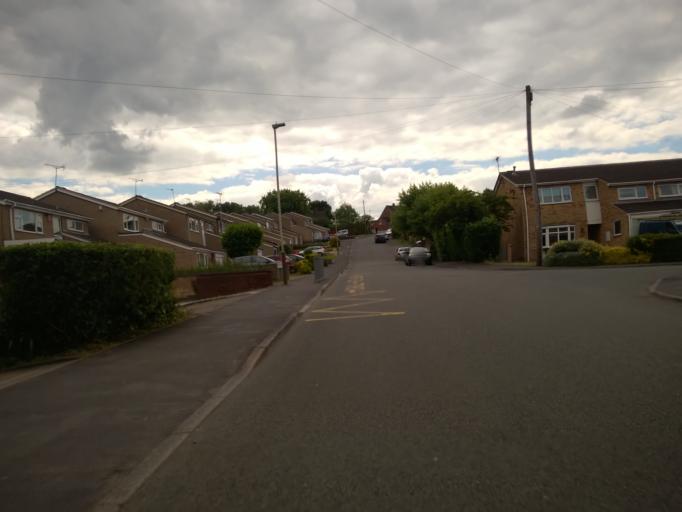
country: GB
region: England
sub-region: Leicestershire
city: Glenfield
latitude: 52.6478
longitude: -1.1662
